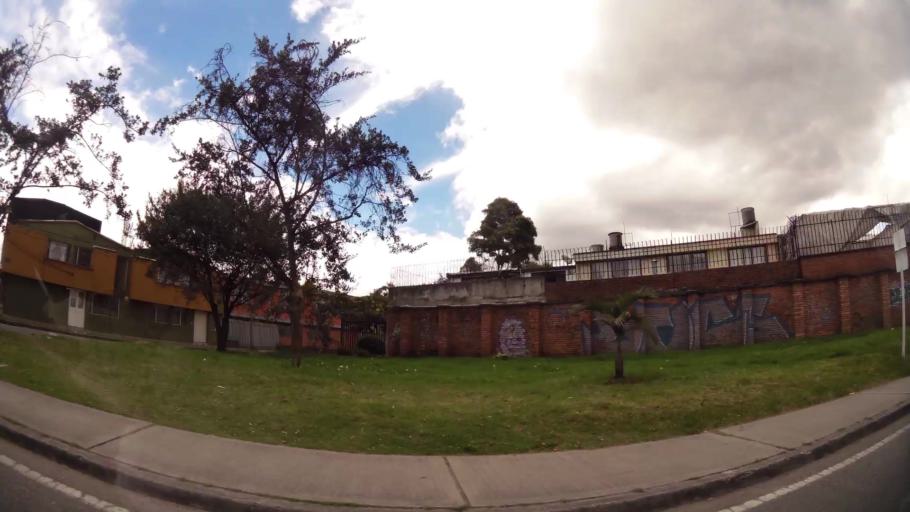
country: CO
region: Bogota D.C.
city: Bogota
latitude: 4.6656
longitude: -74.1092
